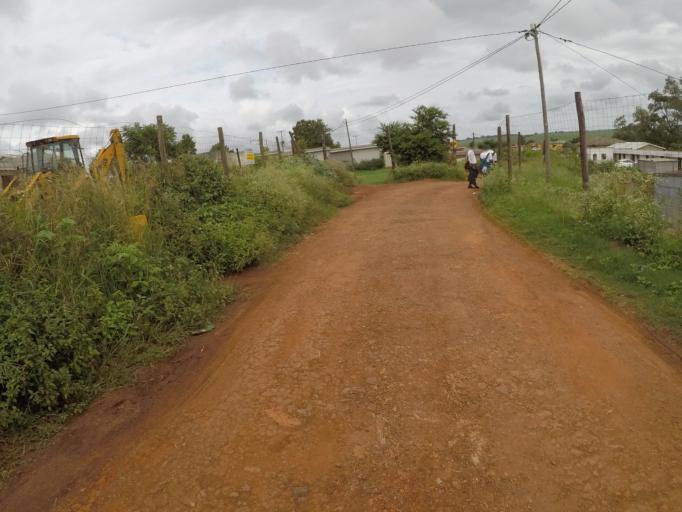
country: ZA
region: KwaZulu-Natal
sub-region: uThungulu District Municipality
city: Empangeni
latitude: -28.7777
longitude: 31.8726
